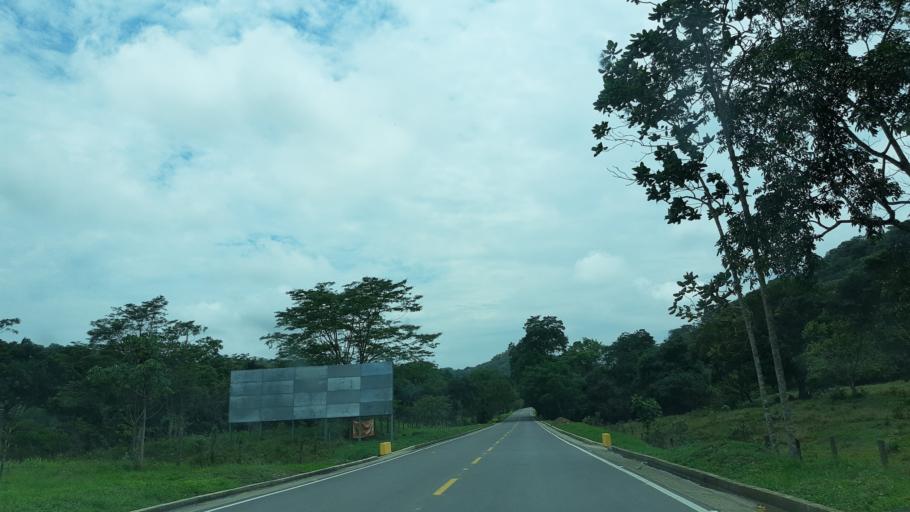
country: CO
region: Boyaca
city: San Luis de Gaceno
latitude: 4.8303
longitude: -73.1436
